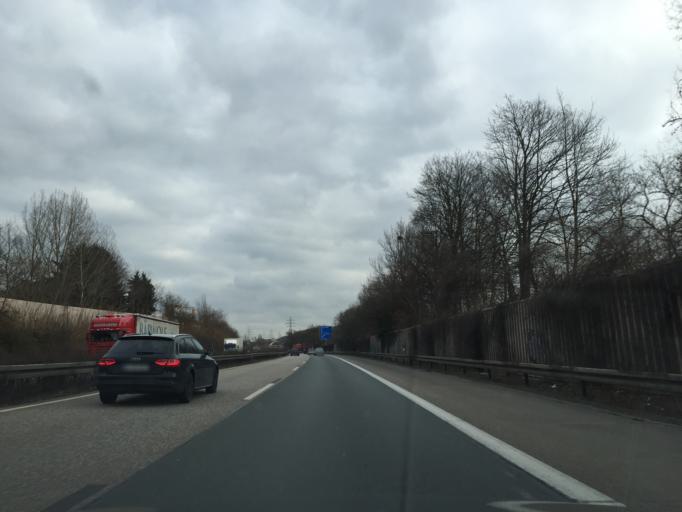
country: DE
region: North Rhine-Westphalia
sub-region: Regierungsbezirk Arnsberg
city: Nachrodt-Wiblingwerde
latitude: 51.3655
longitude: 7.5630
